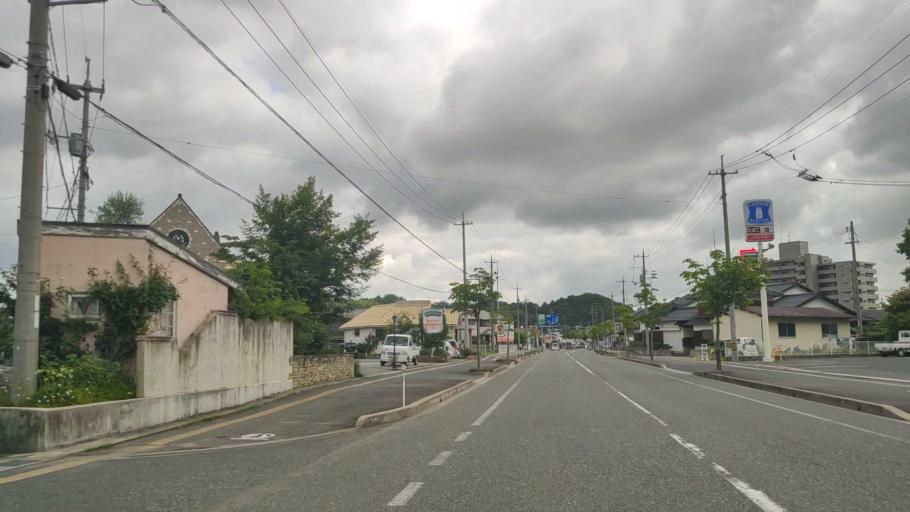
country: JP
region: Tottori
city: Yonago
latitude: 35.4231
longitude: 133.3438
